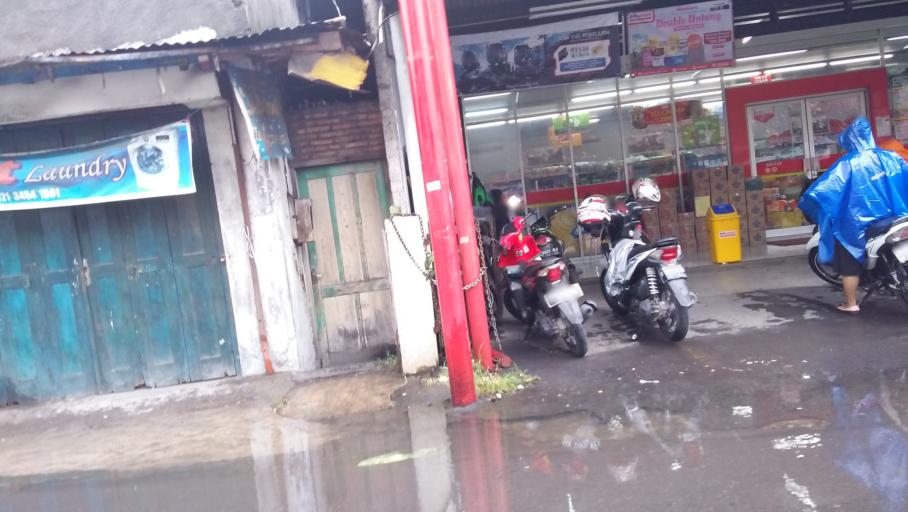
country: ID
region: Daerah Istimewa Yogyakarta
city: Depok
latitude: -7.7828
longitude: 110.3996
